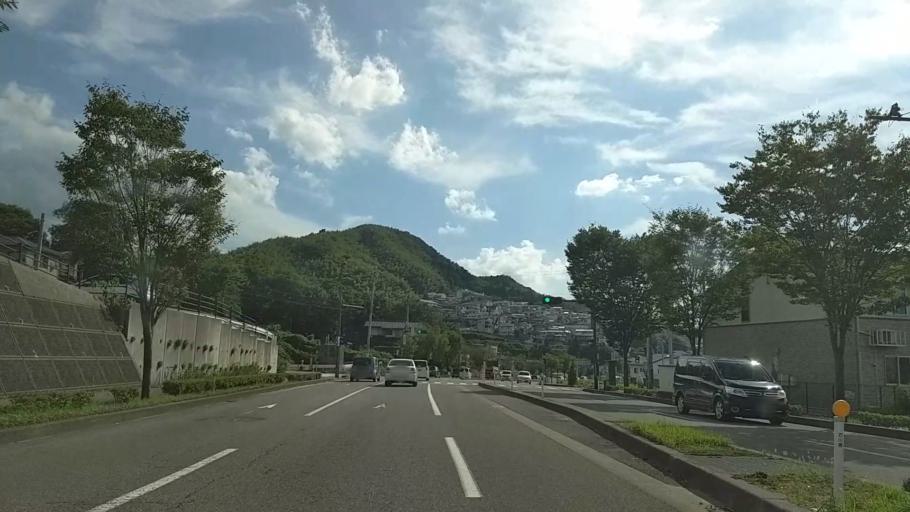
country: JP
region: Ishikawa
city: Nonoichi
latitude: 36.5296
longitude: 136.6522
